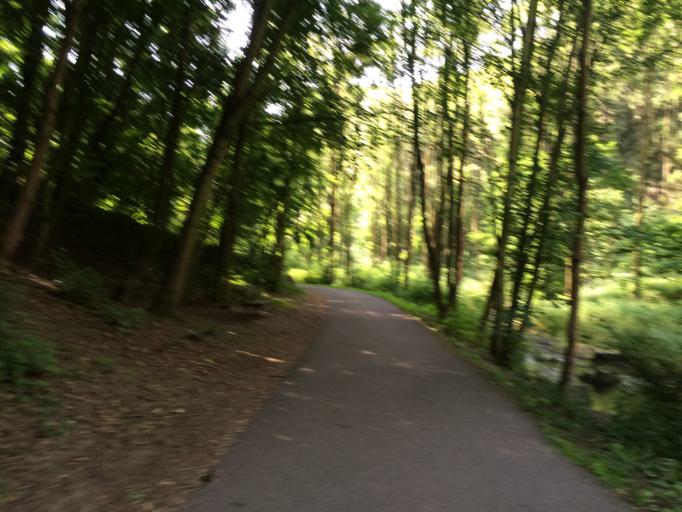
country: CZ
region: Central Bohemia
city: Horomerice
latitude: 50.0959
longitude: 14.3162
